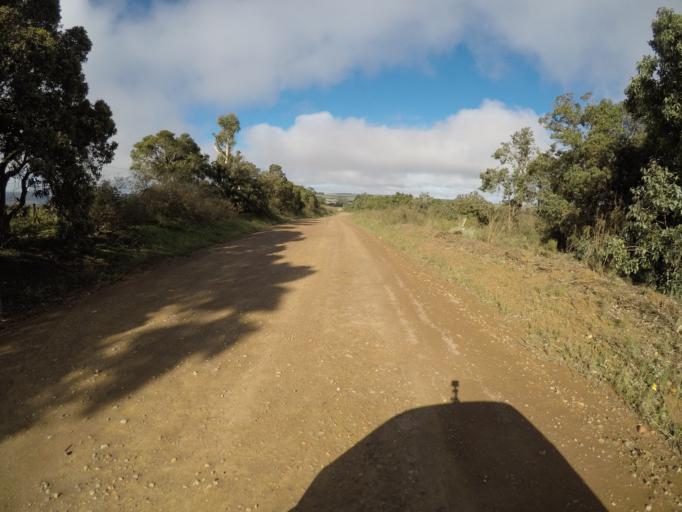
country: ZA
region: Western Cape
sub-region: Cape Winelands District Municipality
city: Ashton
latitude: -34.1169
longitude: 19.8048
